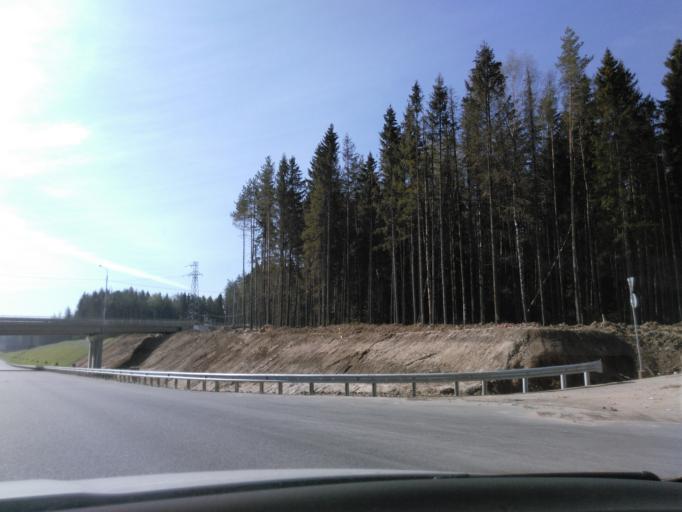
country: RU
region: Moskovskaya
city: Skhodnya
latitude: 55.9822
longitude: 37.3121
